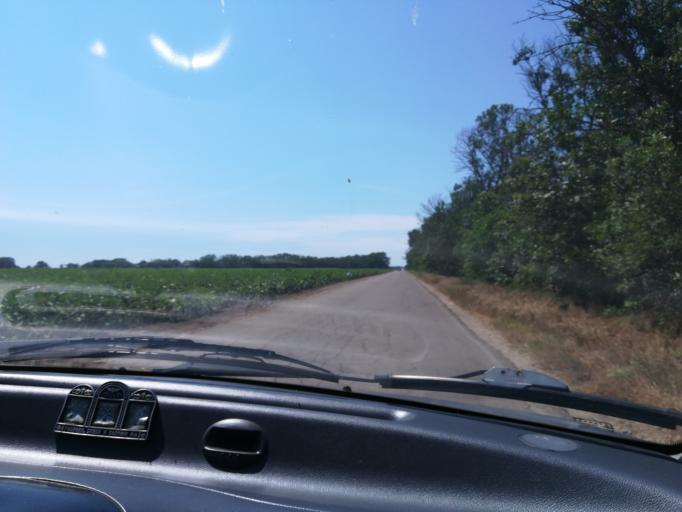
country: RU
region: Krasnodarskiy
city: Blagovetschenskaya
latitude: 45.0576
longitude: 37.1053
